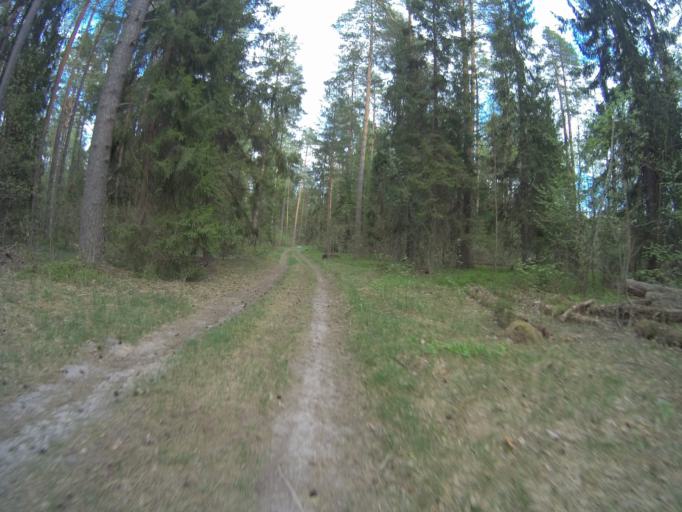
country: RU
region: Vladimir
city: Orgtrud
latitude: 56.1178
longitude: 40.7160
